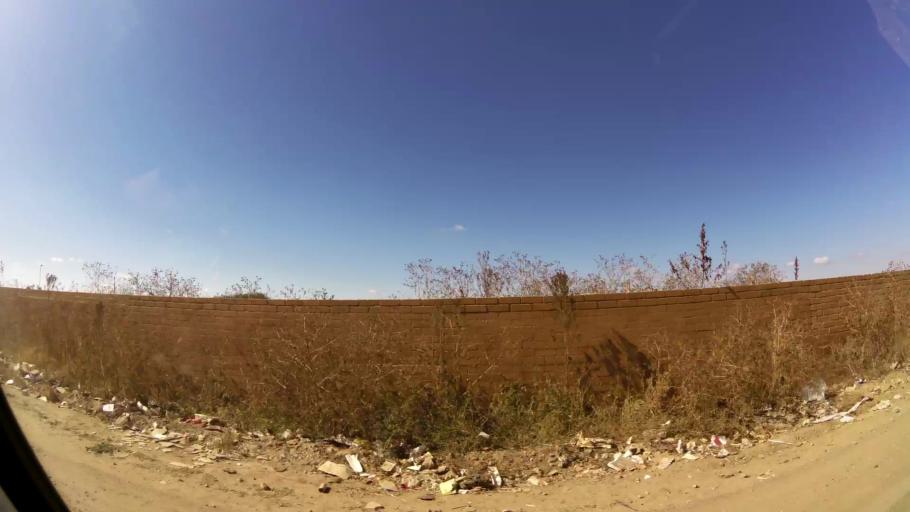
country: ZA
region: Limpopo
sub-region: Capricorn District Municipality
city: Polokwane
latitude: -23.8725
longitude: 29.4253
